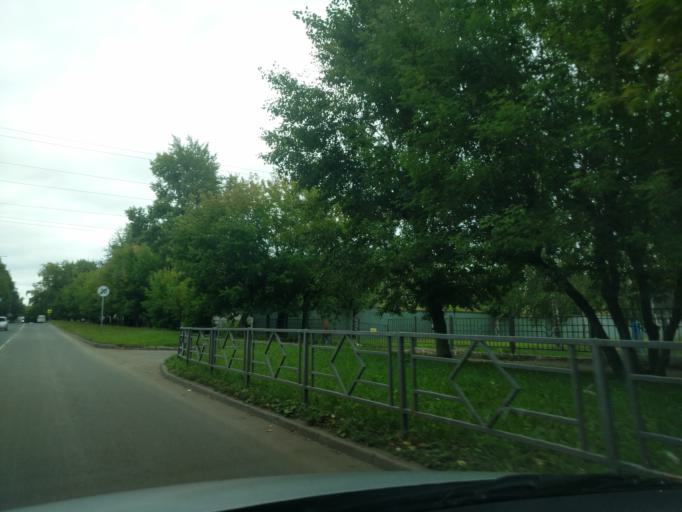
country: RU
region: Kirov
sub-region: Kirovo-Chepetskiy Rayon
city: Kirov
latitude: 58.6355
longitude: 49.6152
